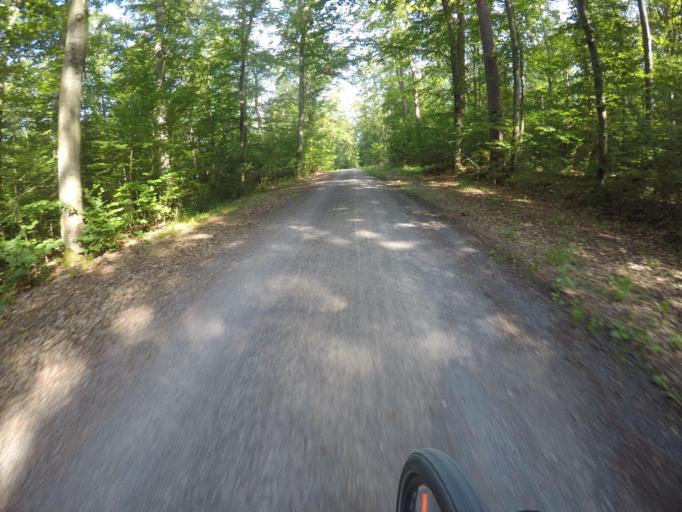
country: DE
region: Baden-Wuerttemberg
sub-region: Regierungsbezirk Stuttgart
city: Weissach
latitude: 48.8671
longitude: 8.9035
